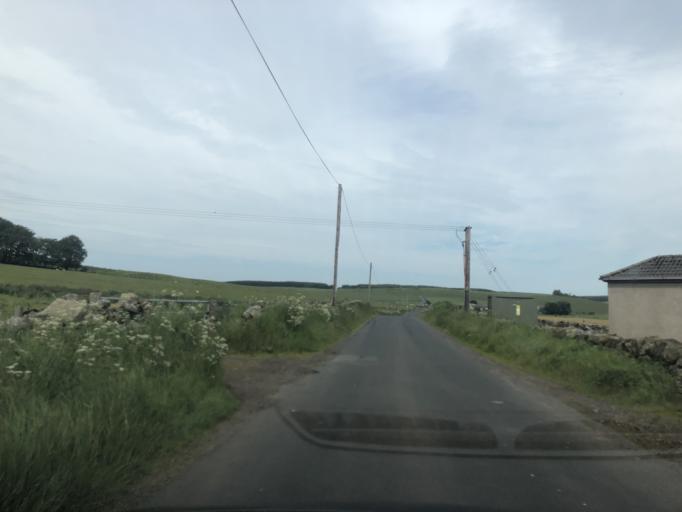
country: GB
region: Scotland
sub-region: The Scottish Borders
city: West Linton
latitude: 55.7597
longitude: -3.3379
